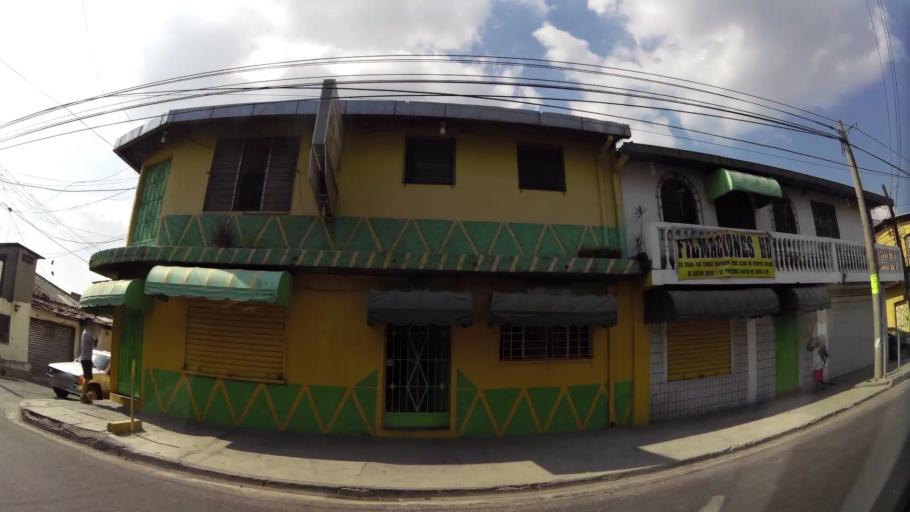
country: SV
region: San Salvador
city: Delgado
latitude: 13.7109
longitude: -89.1725
